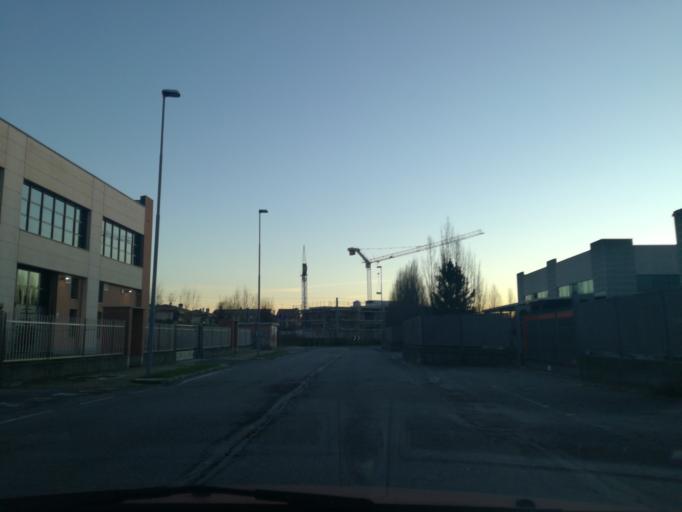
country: IT
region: Lombardy
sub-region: Provincia di Lecco
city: Osnago
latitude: 45.6707
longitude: 9.3945
